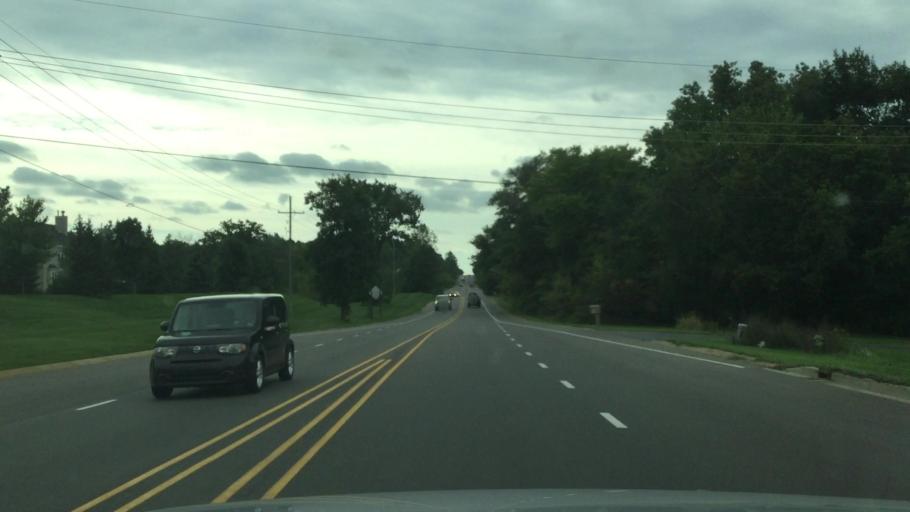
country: US
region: Michigan
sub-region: Livingston County
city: Howell
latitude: 42.6220
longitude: -83.8752
